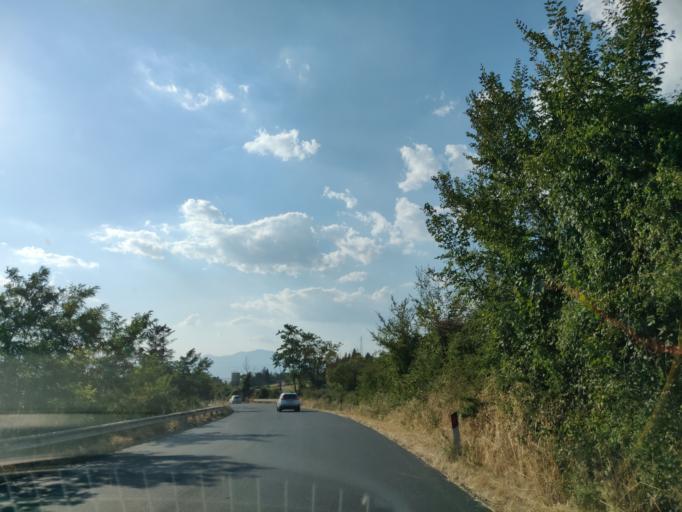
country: IT
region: Latium
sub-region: Provincia di Viterbo
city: Proceno
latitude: 42.7745
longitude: 11.8482
